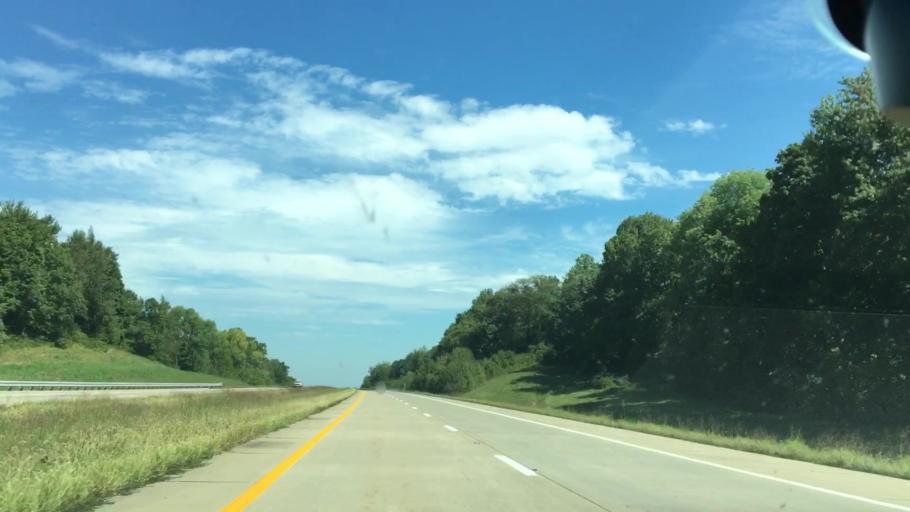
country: US
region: Indiana
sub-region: Warrick County
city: Newburgh
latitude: 37.7594
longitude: -87.3298
